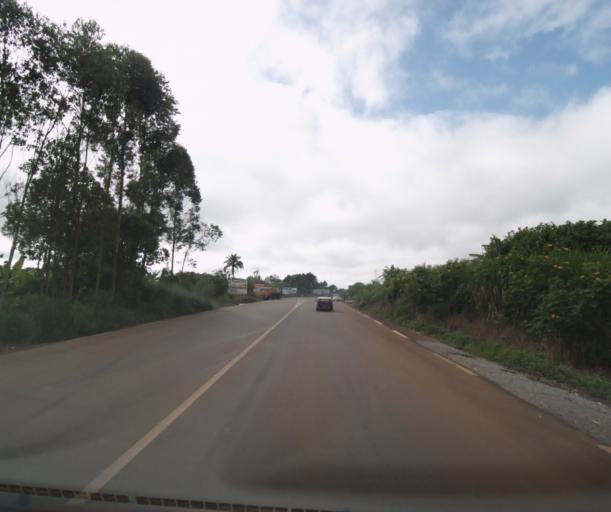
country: CM
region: West
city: Bansoa
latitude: 5.5253
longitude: 10.3401
